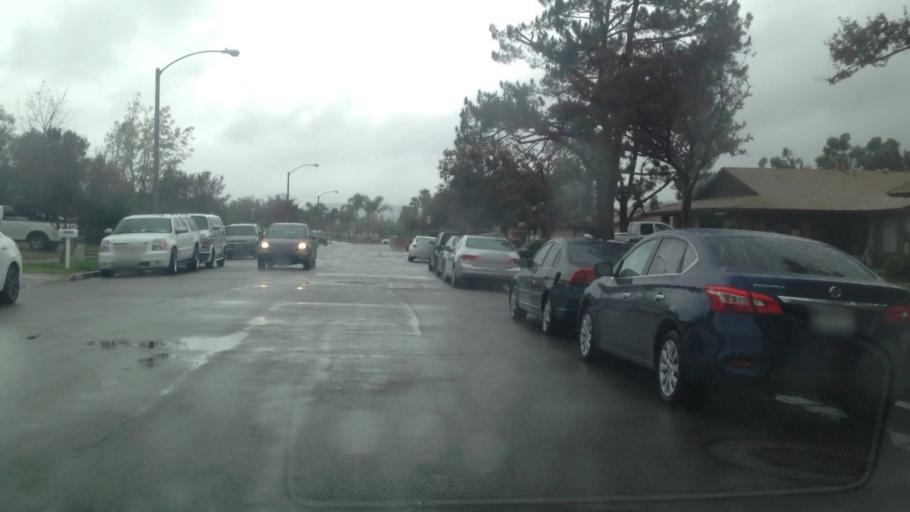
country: US
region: California
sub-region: Riverside County
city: Pedley
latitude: 33.9502
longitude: -117.4608
